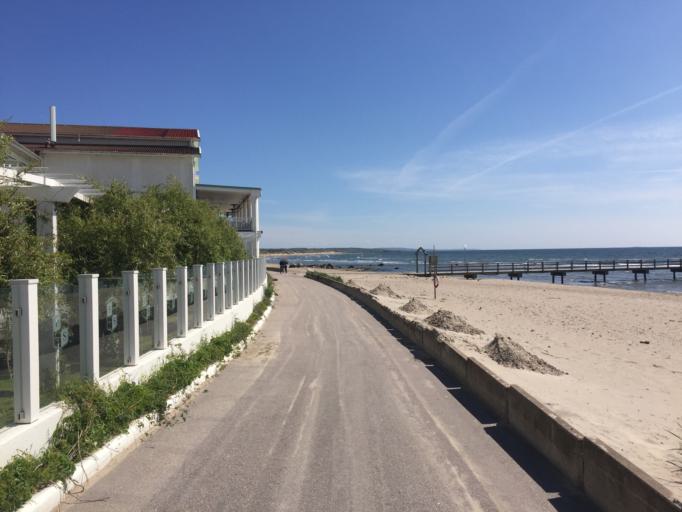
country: SE
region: Halland
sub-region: Falkenbergs Kommun
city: Falkenberg
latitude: 56.8887
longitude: 12.4941
